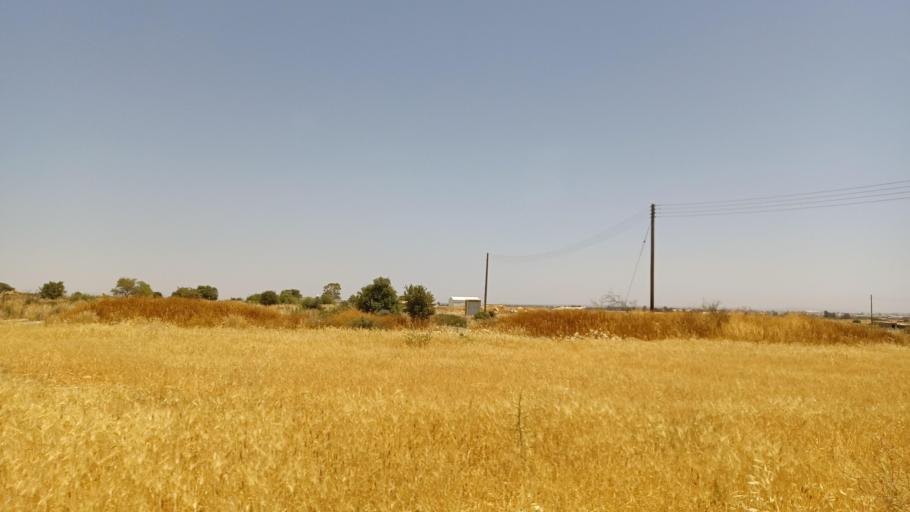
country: CY
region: Larnaka
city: Pergamos
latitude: 35.0234
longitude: 33.7134
